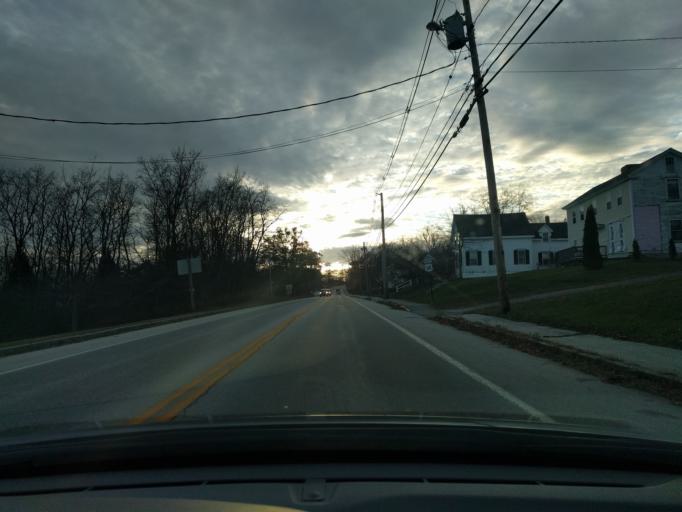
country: US
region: Maine
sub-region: Waldo County
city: Winterport
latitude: 44.6330
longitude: -68.8494
